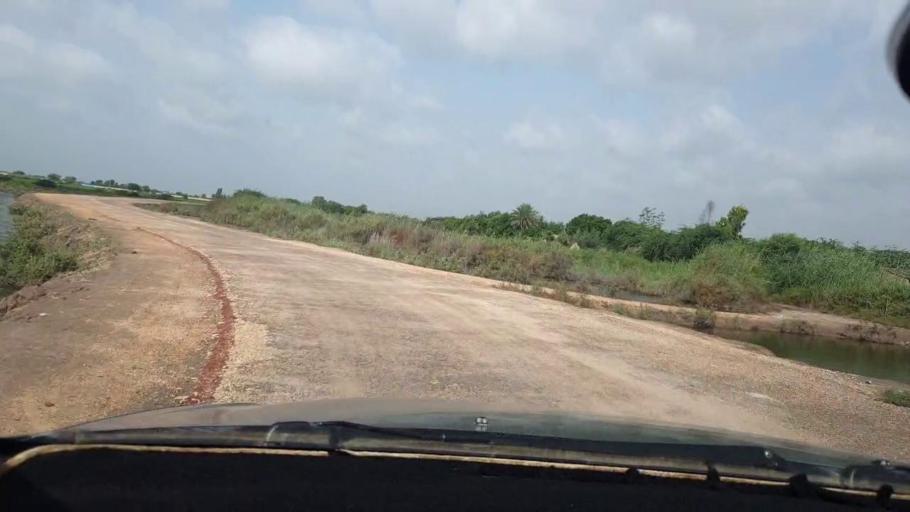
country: PK
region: Sindh
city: Tando Bago
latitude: 24.7812
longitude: 68.9817
